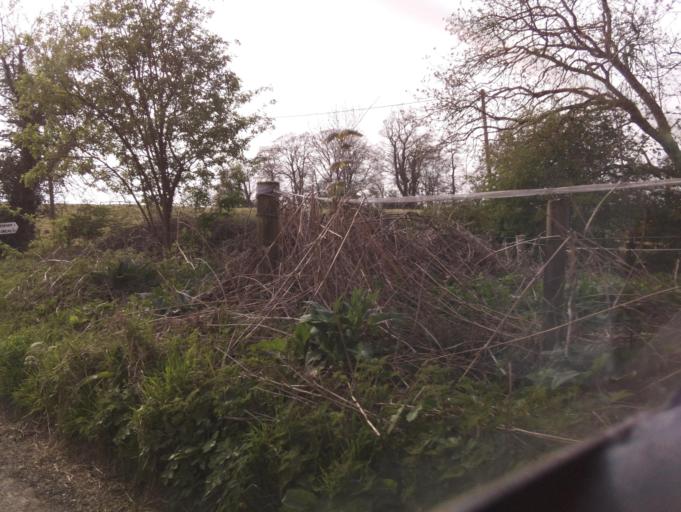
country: GB
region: England
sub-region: Dorset
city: Sherborne
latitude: 50.9937
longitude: -2.5155
